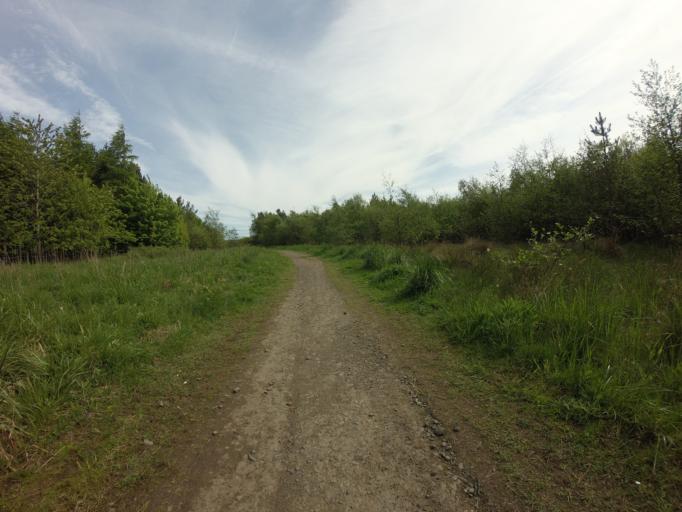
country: GB
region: Scotland
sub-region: West Lothian
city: Mid Calder
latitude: 55.9137
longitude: -3.4933
